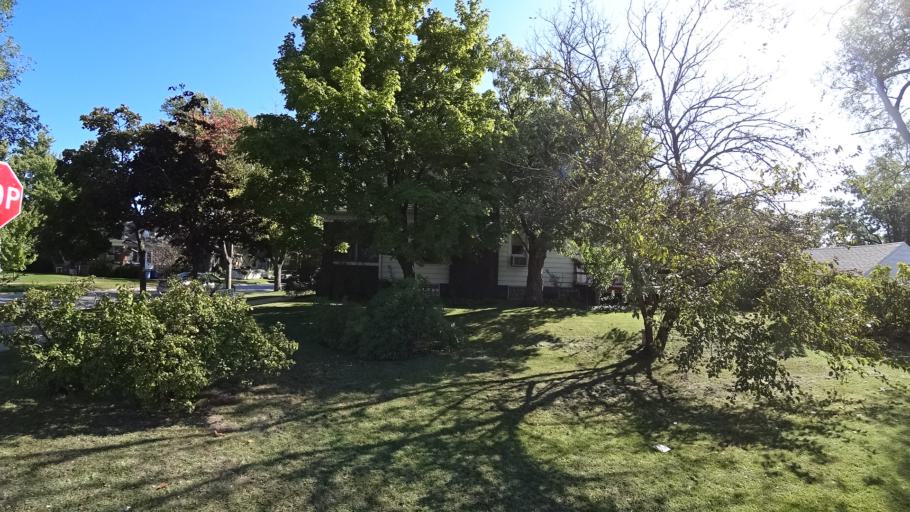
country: US
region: Indiana
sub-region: LaPorte County
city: Michigan City
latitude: 41.7074
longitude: -86.8907
